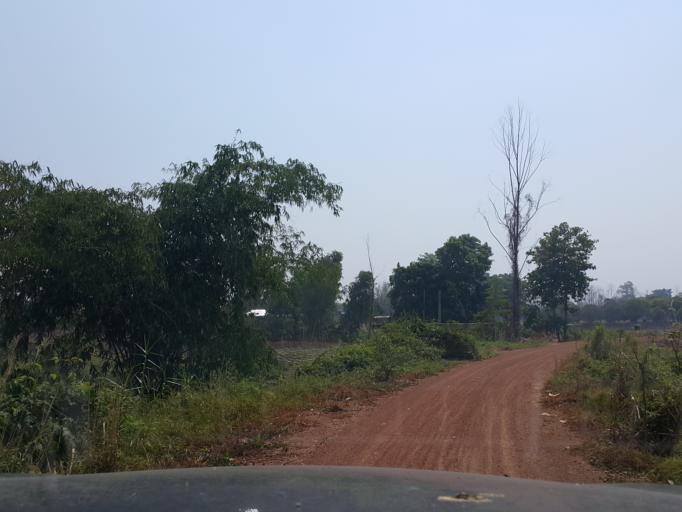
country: TH
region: Sukhothai
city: Thung Saliam
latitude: 17.3151
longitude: 99.5600
